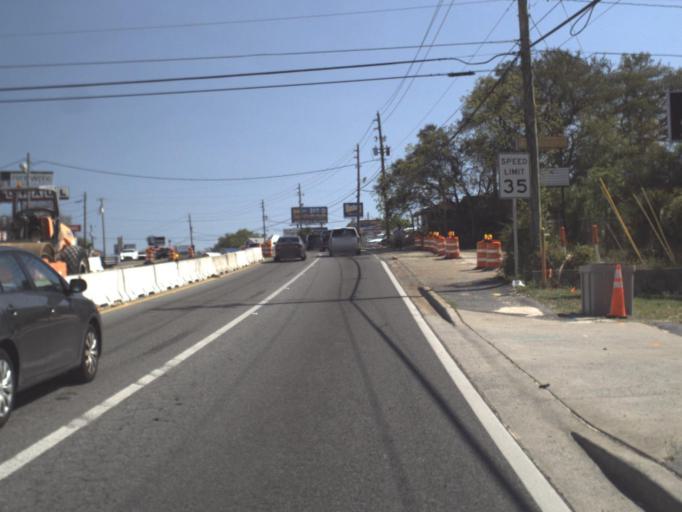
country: US
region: Florida
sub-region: Okaloosa County
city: Wright
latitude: 30.4316
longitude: -86.6397
